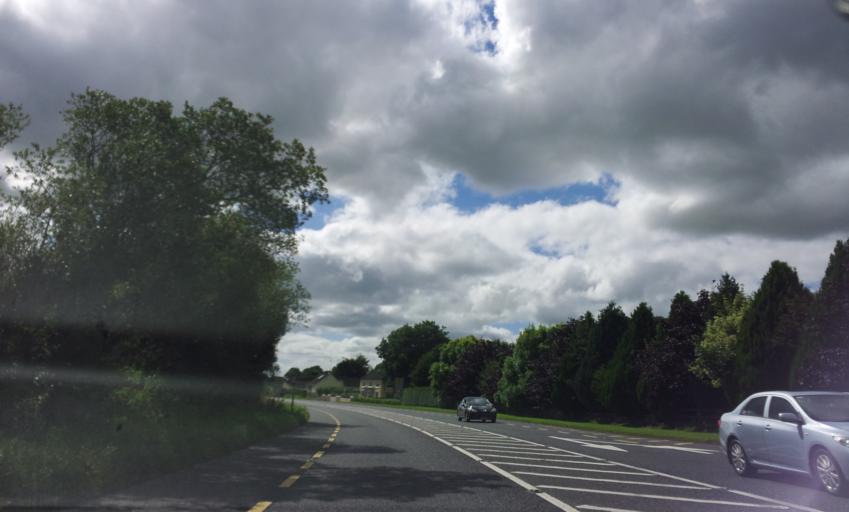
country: IE
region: Munster
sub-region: County Cork
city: Killumney
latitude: 51.8762
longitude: -8.7084
